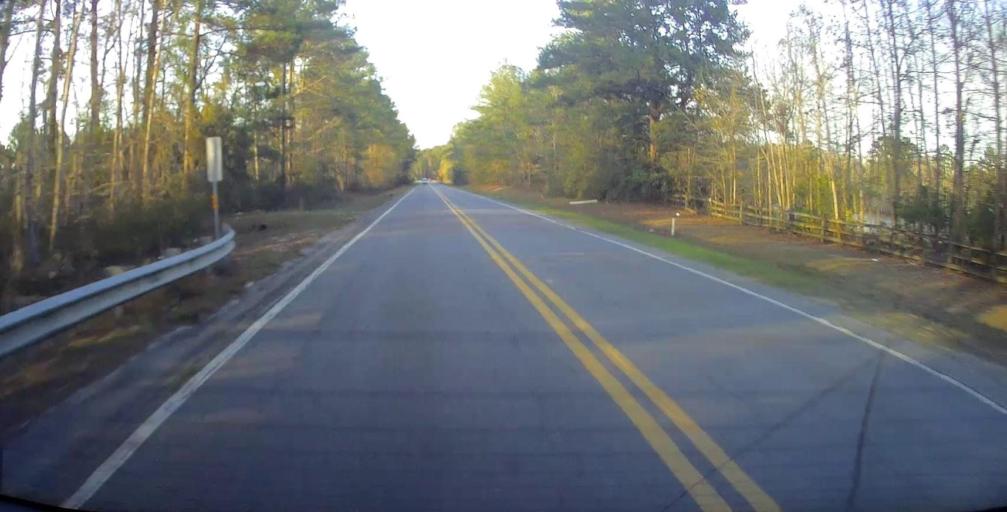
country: US
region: Georgia
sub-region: Chatham County
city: Bloomingdale
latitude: 32.1602
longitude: -81.3861
